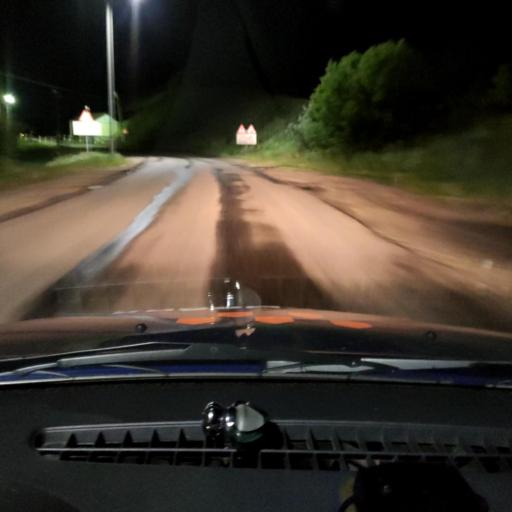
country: RU
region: Voronezj
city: Khrenovoye
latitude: 51.1186
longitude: 40.2638
